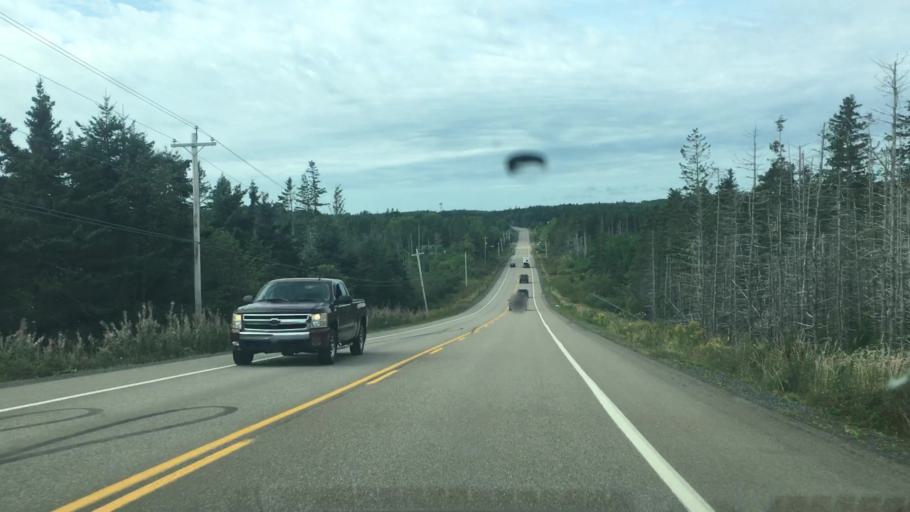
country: CA
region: Nova Scotia
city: Princeville
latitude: 45.6941
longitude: -60.7387
